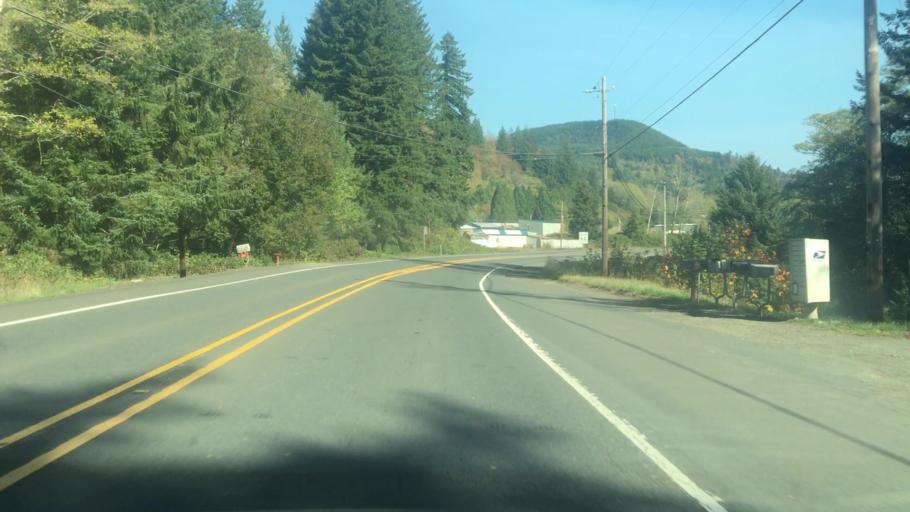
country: US
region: Oregon
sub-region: Lincoln County
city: Rose Lodge
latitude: 45.0207
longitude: -123.8628
